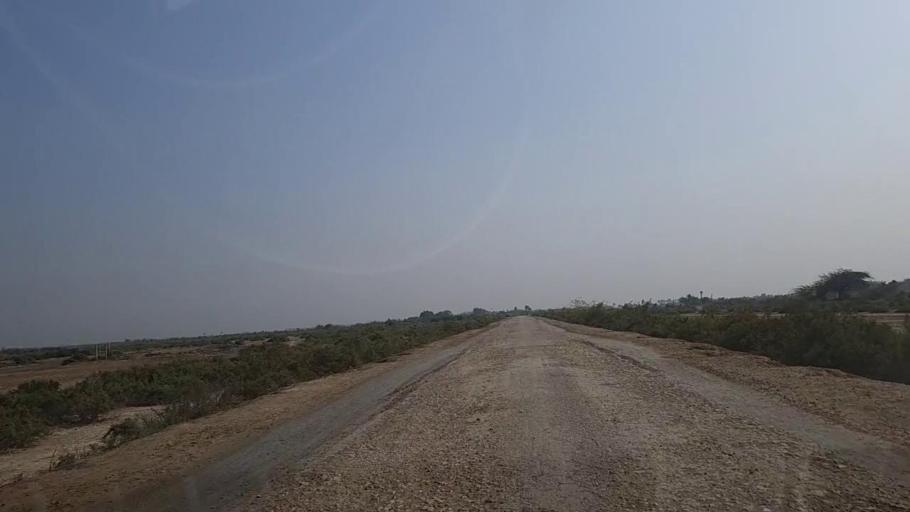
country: PK
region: Sindh
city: Keti Bandar
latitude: 24.2532
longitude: 67.6260
